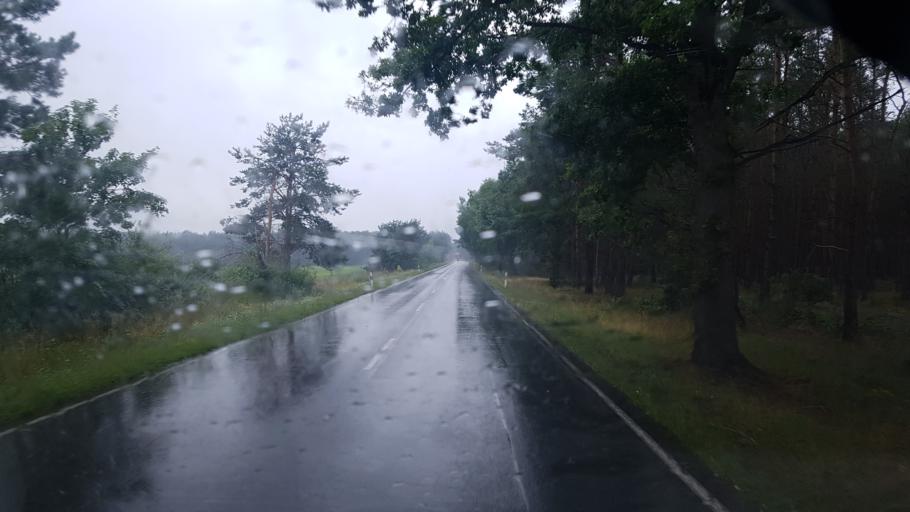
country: DE
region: Brandenburg
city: Golssen
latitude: 52.0505
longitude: 13.5888
